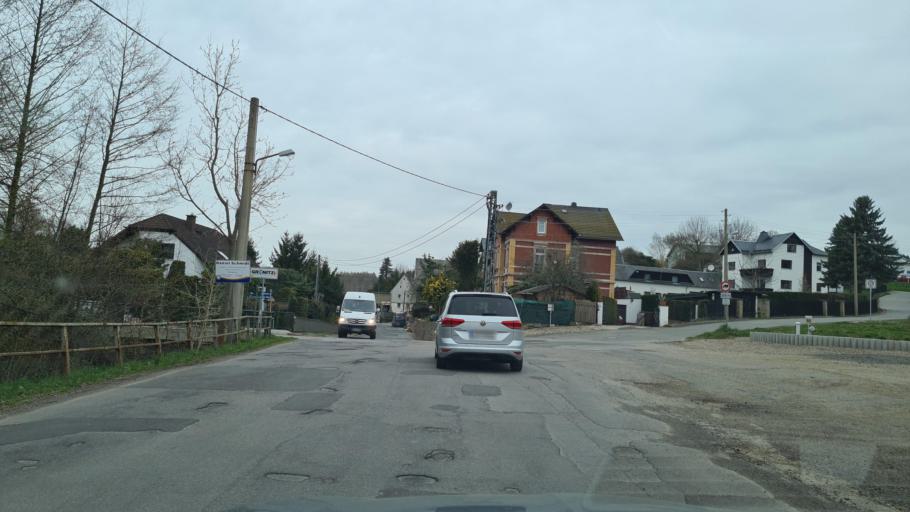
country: DE
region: Saxony
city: Claussnitz
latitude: 50.9018
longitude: 12.9114
